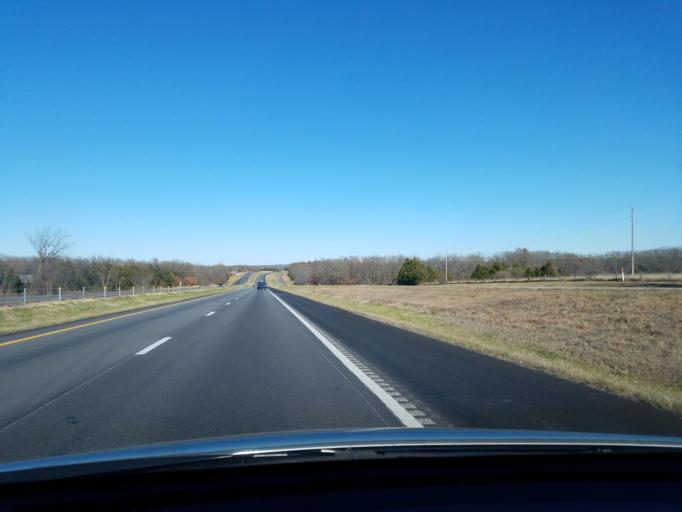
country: US
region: Missouri
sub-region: Webster County
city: Marshfield
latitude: 37.3911
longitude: -92.8997
